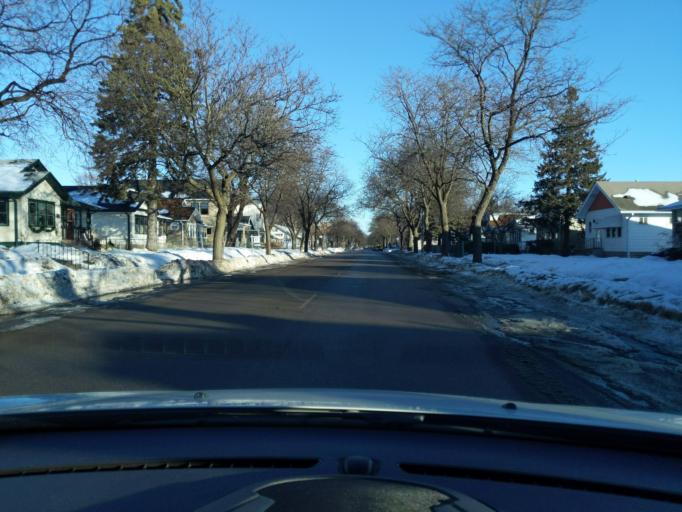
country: US
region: Minnesota
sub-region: Ramsey County
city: Lauderdale
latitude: 44.9349
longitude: -93.2127
